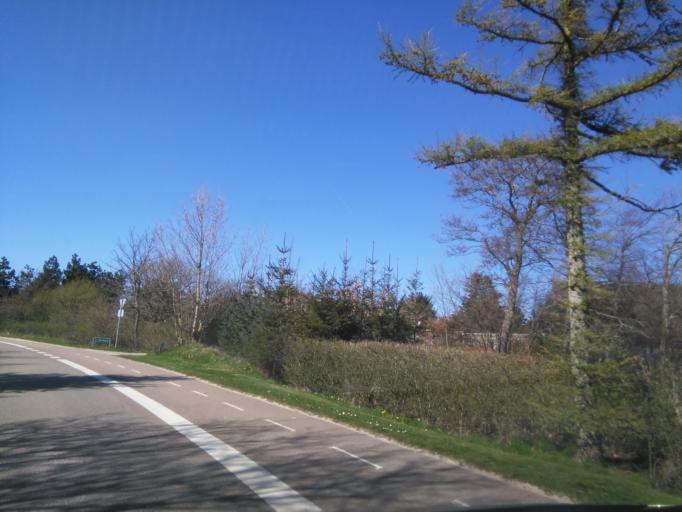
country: DK
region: South Denmark
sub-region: Varde Kommune
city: Oksbol
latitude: 55.5528
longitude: 8.1433
